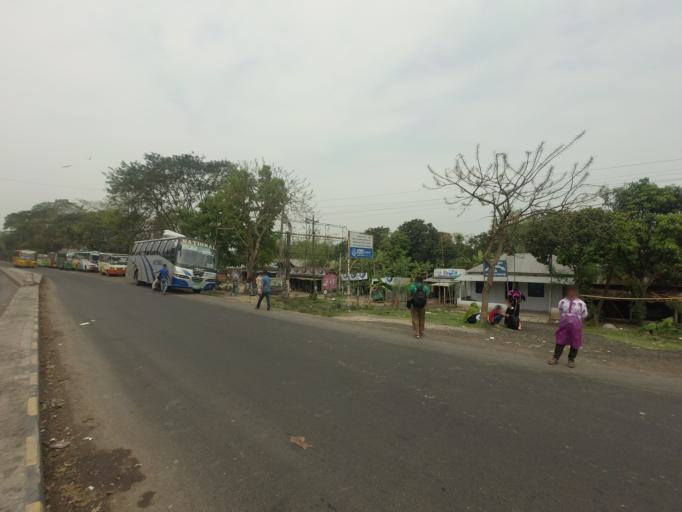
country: BD
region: Rajshahi
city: Sirajganj
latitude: 24.3952
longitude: 89.6909
